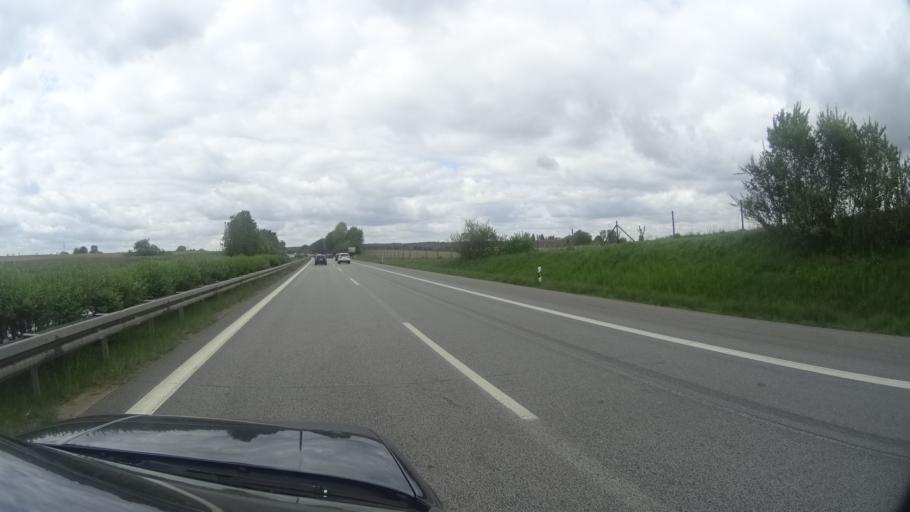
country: DE
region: Mecklenburg-Vorpommern
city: Malchow
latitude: 53.4284
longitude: 12.4216
